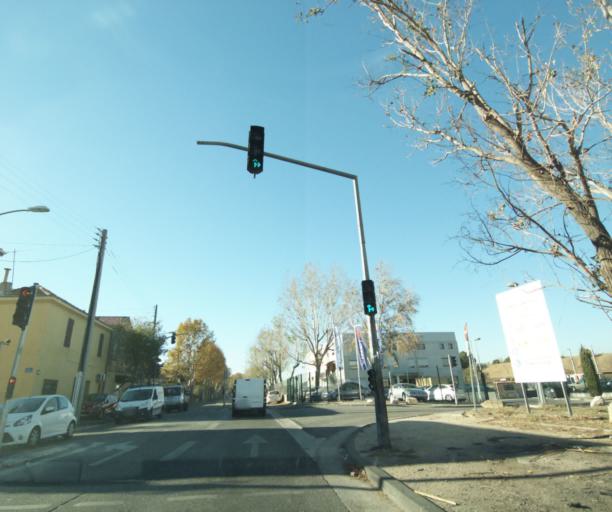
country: FR
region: Provence-Alpes-Cote d'Azur
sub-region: Departement des Bouches-du-Rhone
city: La Penne-sur-Huveaune
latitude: 43.2838
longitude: 5.4939
